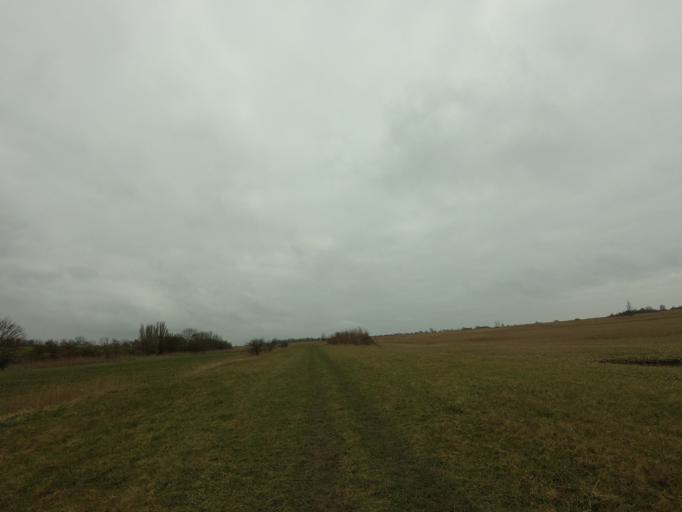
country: NL
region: Friesland
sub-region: Sudwest Fryslan
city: Makkum
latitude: 53.0481
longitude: 5.3973
